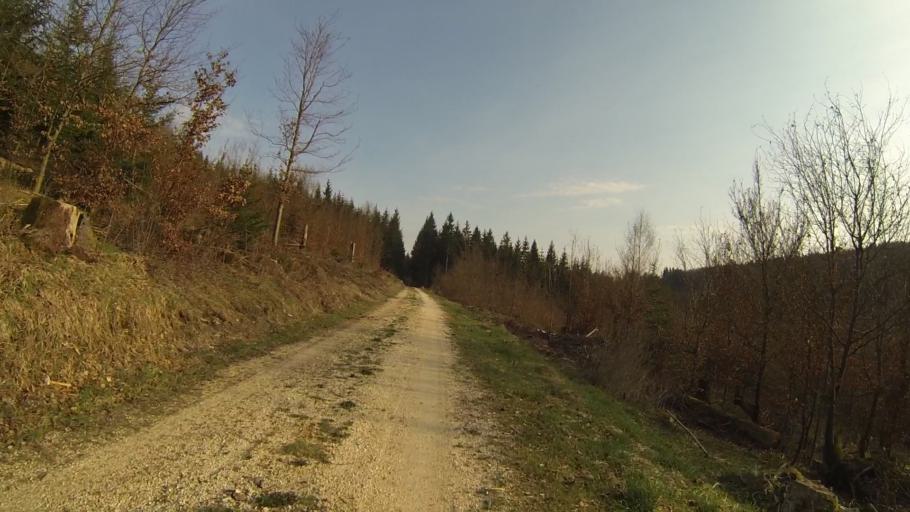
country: DE
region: Baden-Wuerttemberg
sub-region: Regierungsbezirk Stuttgart
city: Bolheim
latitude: 48.6557
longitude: 10.1114
